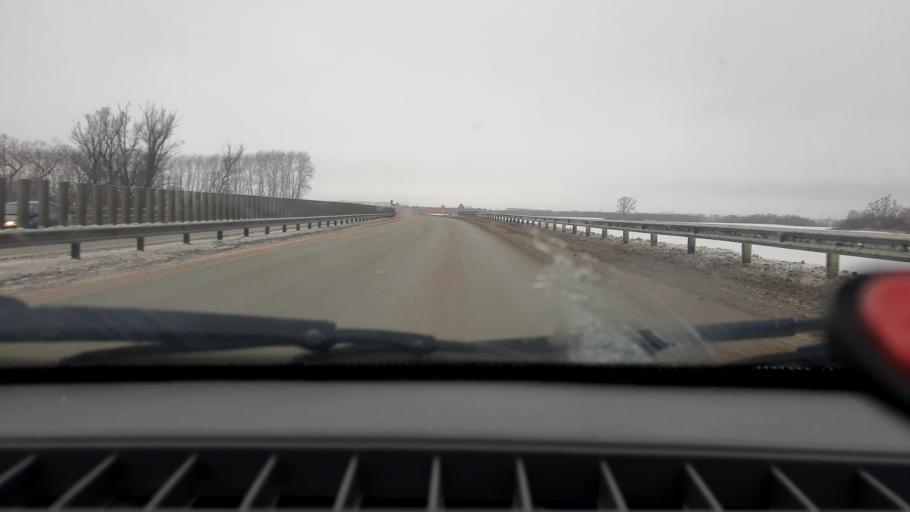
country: RU
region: Bashkortostan
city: Asanovo
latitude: 54.9740
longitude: 55.5744
